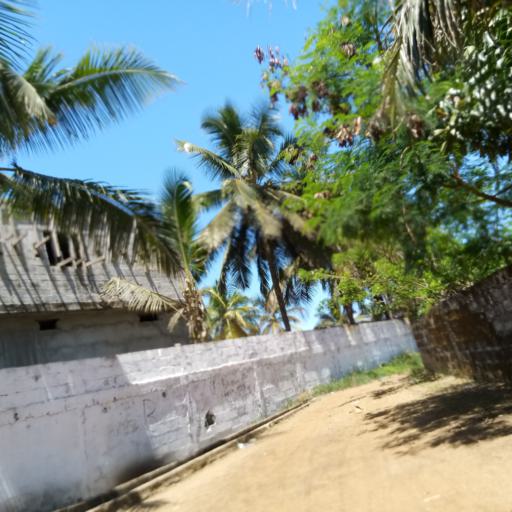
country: LR
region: Montserrado
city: Monrovia
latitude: 6.2352
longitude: -10.6944
